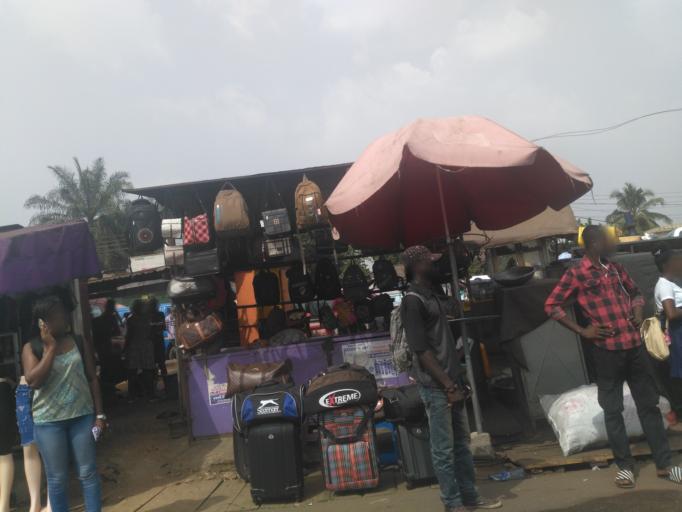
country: GH
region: Ashanti
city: Kumasi
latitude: 6.6870
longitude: -1.5743
